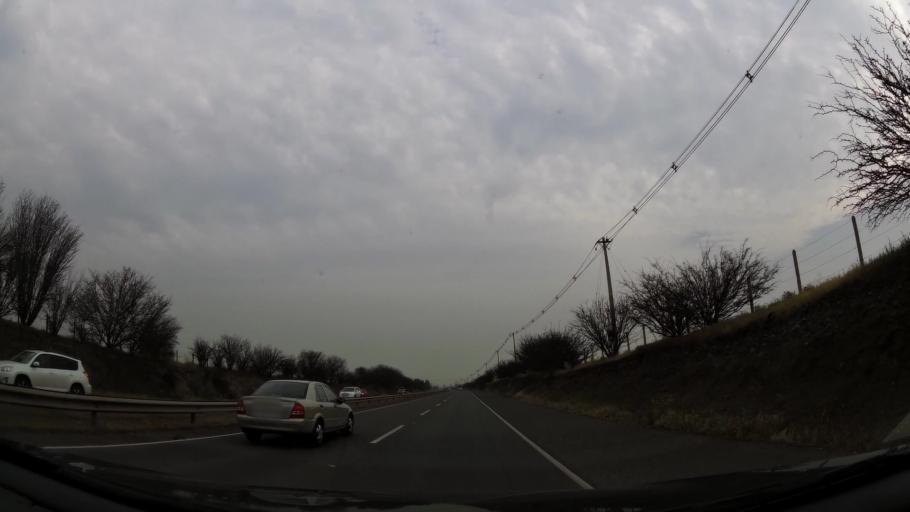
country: CL
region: Santiago Metropolitan
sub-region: Provincia de Chacabuco
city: Chicureo Abajo
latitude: -33.2127
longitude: -70.6721
